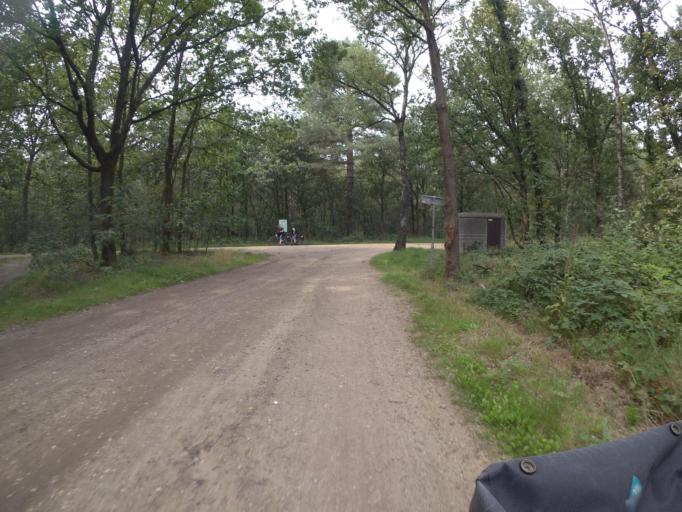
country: NL
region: Limburg
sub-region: Gemeente Bergen
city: Wellerlooi
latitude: 51.5568
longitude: 6.1377
